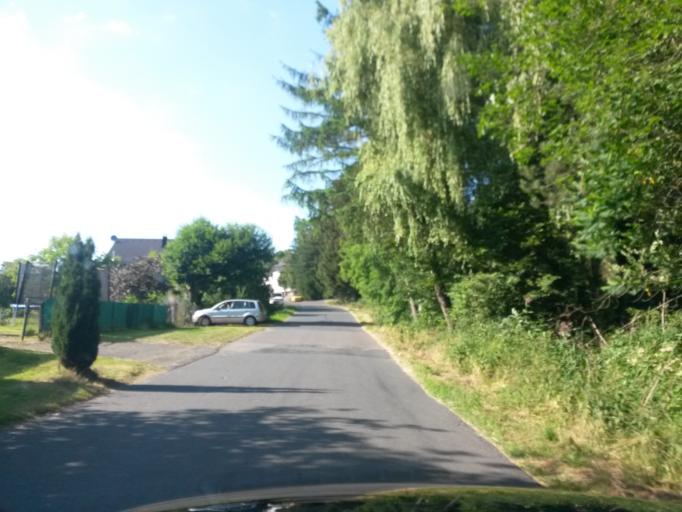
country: DE
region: North Rhine-Westphalia
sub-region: Regierungsbezirk Koln
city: Much
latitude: 50.9328
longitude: 7.4080
